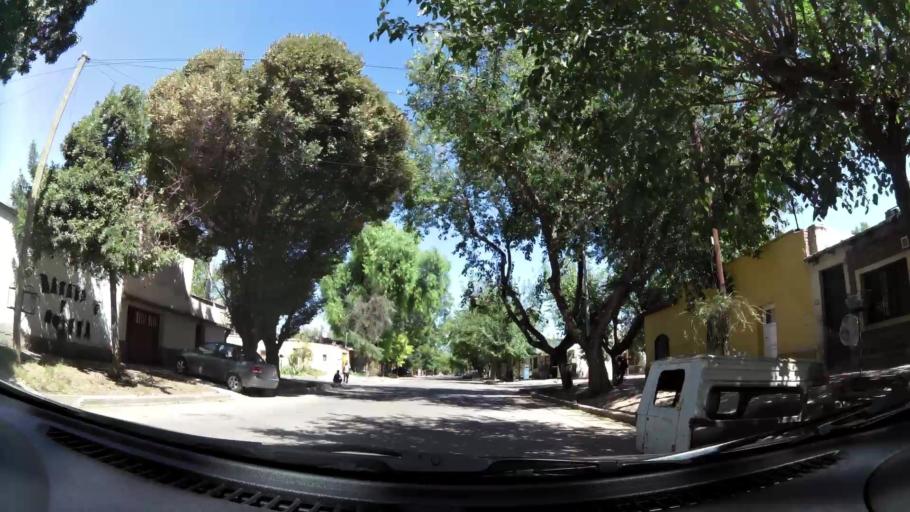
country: AR
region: Mendoza
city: Mendoza
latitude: -32.8763
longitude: -68.8208
